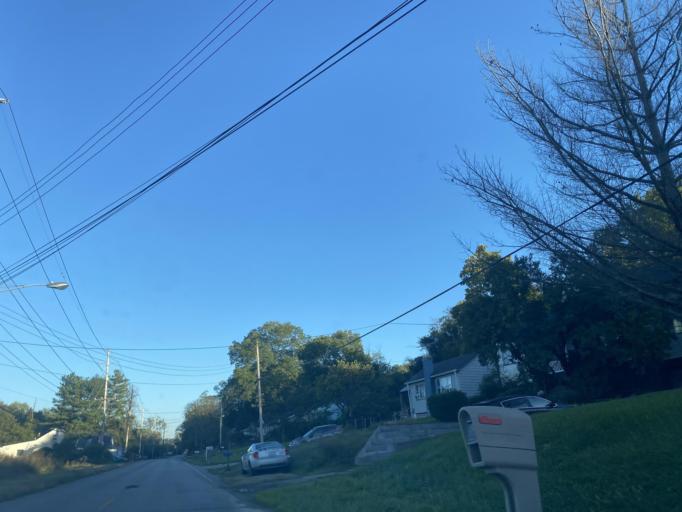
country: US
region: Kentucky
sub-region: Campbell County
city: Dayton
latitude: 39.1135
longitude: -84.4584
